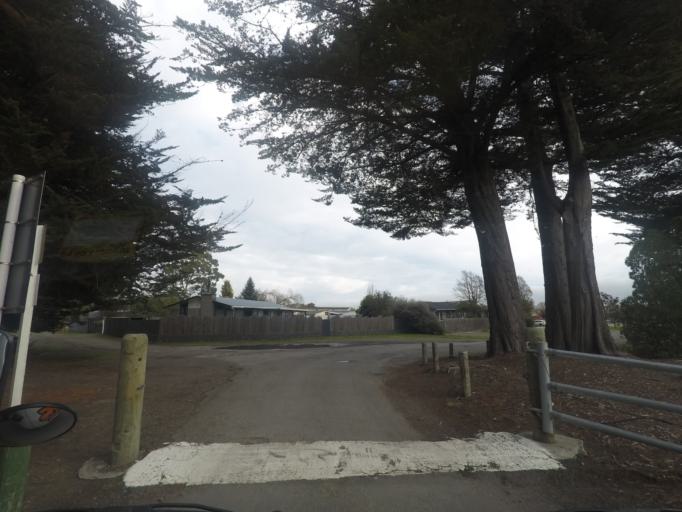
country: NZ
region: Canterbury
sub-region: Waimakariri District
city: Woodend
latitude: -43.2882
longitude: 172.7189
